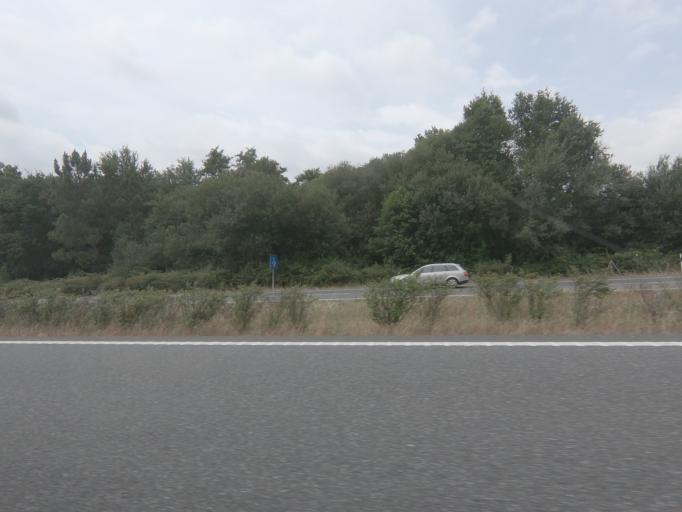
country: ES
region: Galicia
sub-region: Provincia de Pontevedra
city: Ponteareas
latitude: 42.1551
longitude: -8.4918
